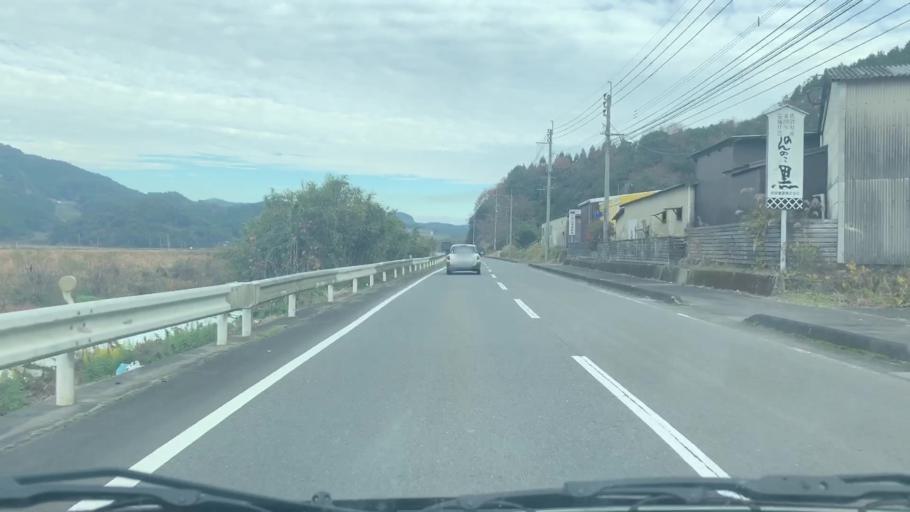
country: JP
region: Saga Prefecture
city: Imaricho-ko
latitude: 33.2740
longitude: 129.9648
